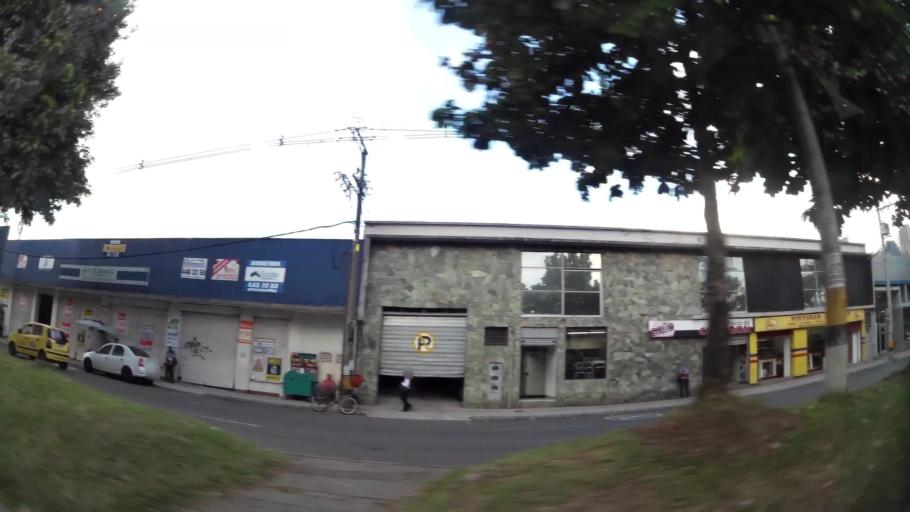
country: CO
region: Antioquia
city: Medellin
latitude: 6.2299
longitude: -75.5727
